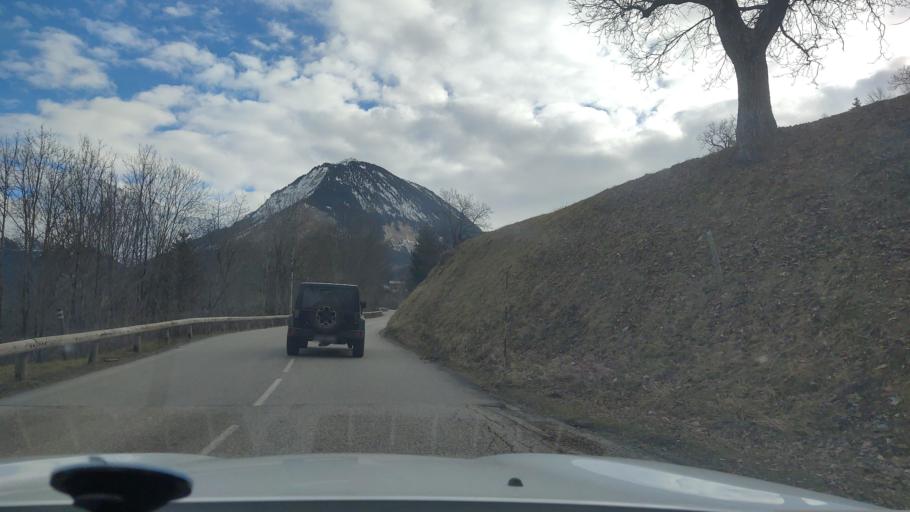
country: FR
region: Rhone-Alpes
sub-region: Departement de la Savoie
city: Saint-Bon-Tarentaise
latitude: 45.4380
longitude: 6.6298
